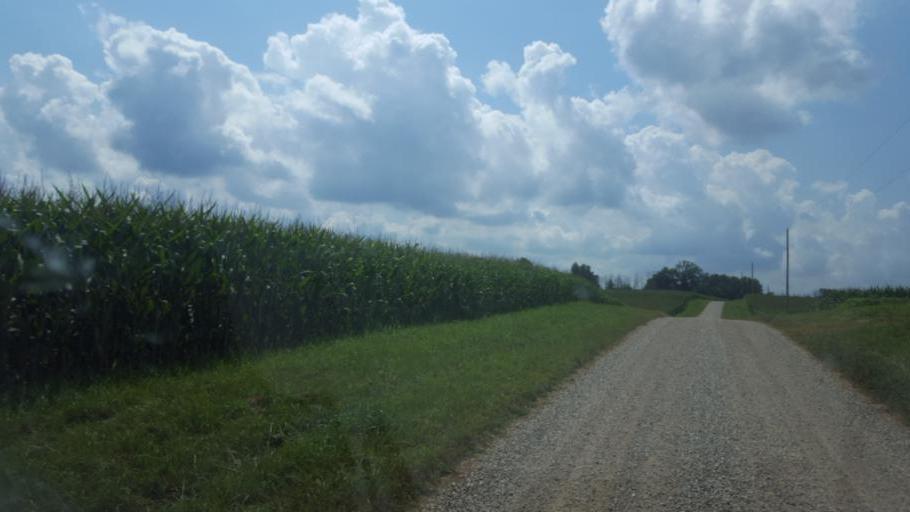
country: US
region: Ohio
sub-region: Knox County
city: Fredericktown
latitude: 40.4521
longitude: -82.6422
